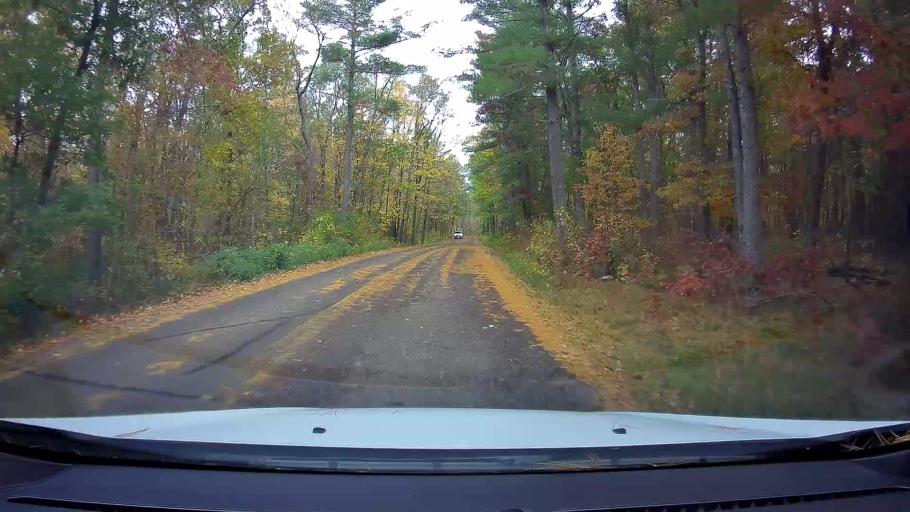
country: US
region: Wisconsin
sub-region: Polk County
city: Saint Croix Falls
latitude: 45.3893
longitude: -92.6549
